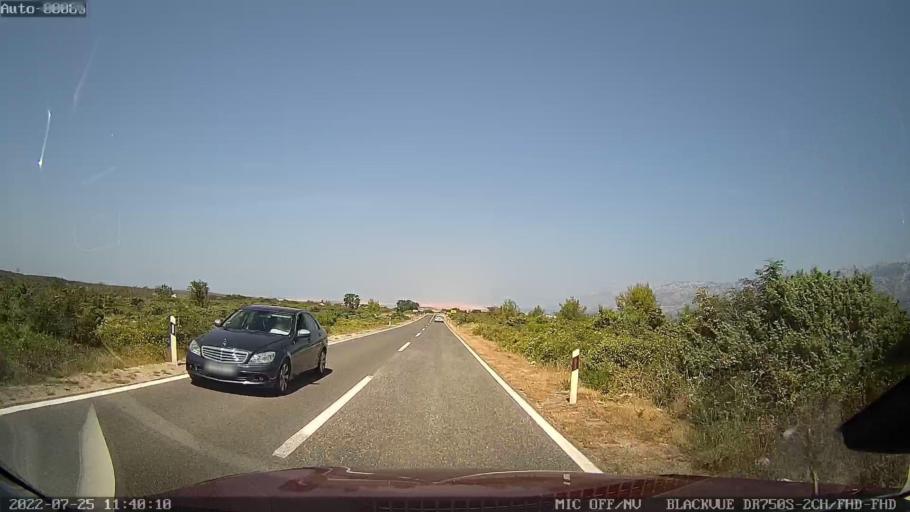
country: HR
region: Zadarska
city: Razanac
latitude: 44.2613
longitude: 15.3638
